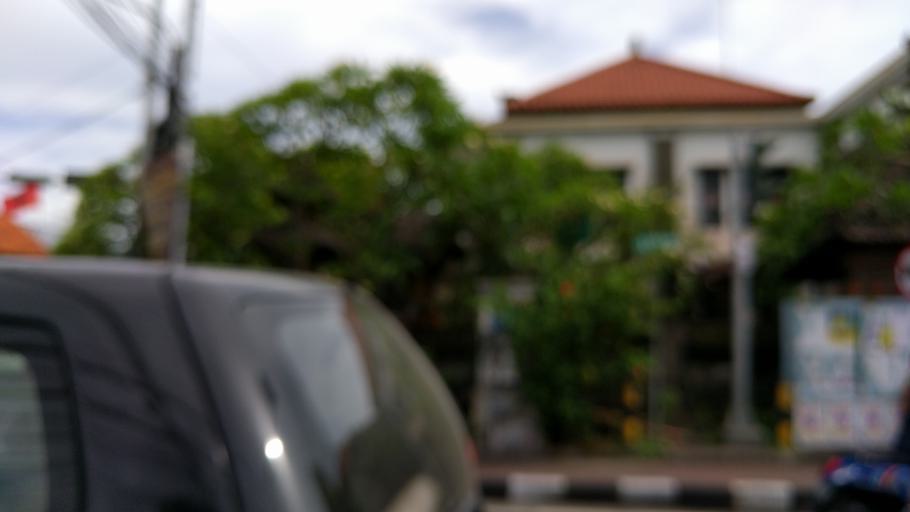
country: ID
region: Bali
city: Kuta
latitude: -8.6721
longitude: 115.1648
